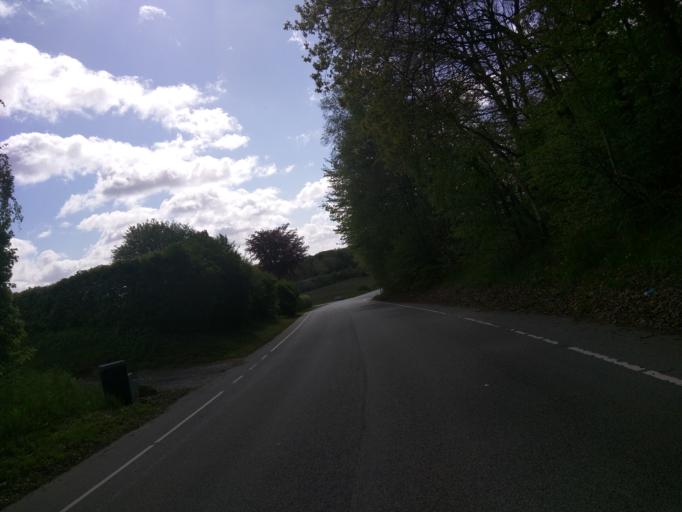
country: DK
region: Central Jutland
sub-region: Viborg Kommune
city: Viborg
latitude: 56.4059
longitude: 9.4281
